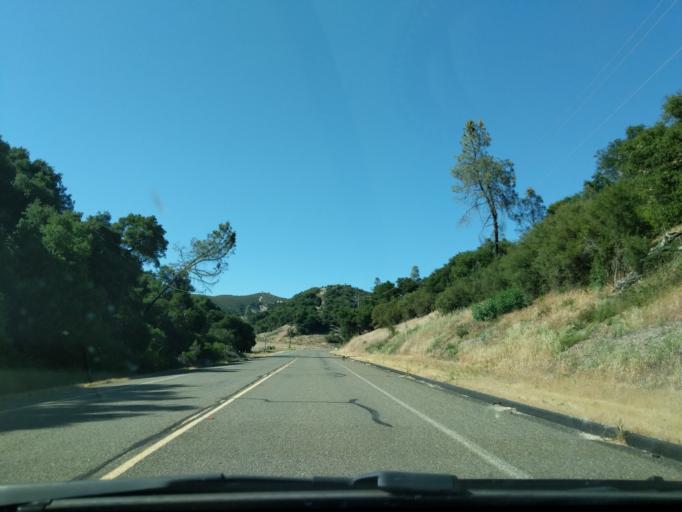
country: US
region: California
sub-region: Monterey County
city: King City
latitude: 36.0667
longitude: -121.1843
